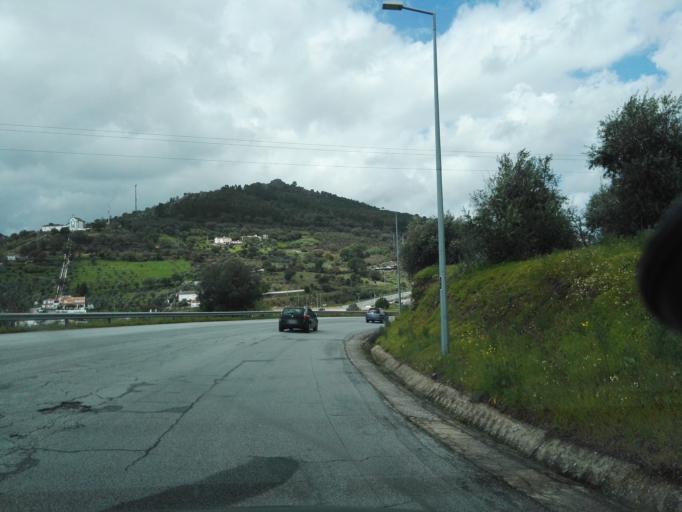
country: PT
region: Portalegre
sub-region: Portalegre
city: Portalegre
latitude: 39.2966
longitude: -7.4352
